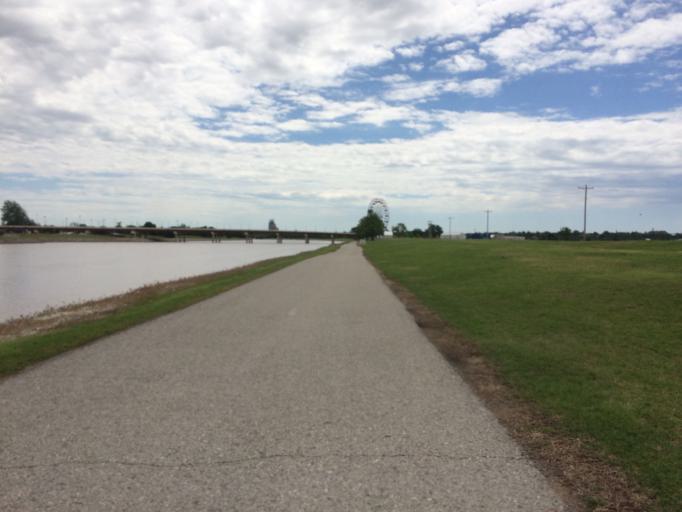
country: US
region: Oklahoma
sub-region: Oklahoma County
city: Oklahoma City
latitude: 35.4551
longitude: -97.5346
